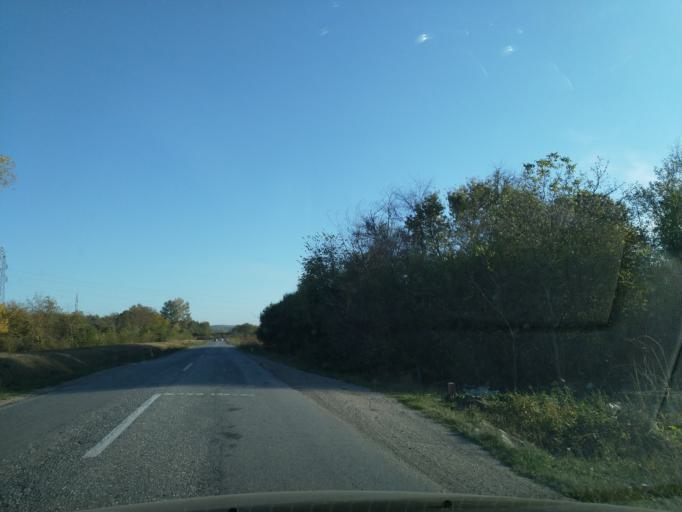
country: RS
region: Central Serbia
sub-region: Pomoravski Okrug
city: Svilajnac
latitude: 44.2261
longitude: 21.1472
